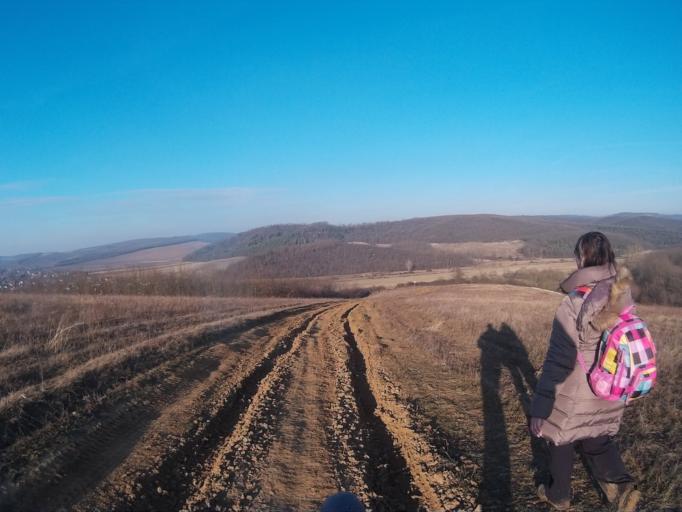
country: HU
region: Nograd
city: Bercel
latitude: 47.9713
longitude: 19.4389
